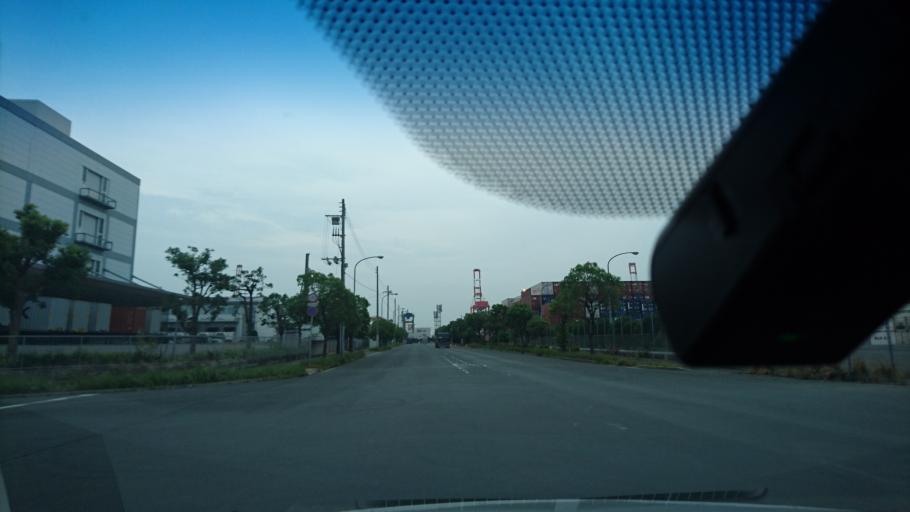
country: JP
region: Hyogo
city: Ashiya
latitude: 34.6848
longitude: 135.2576
